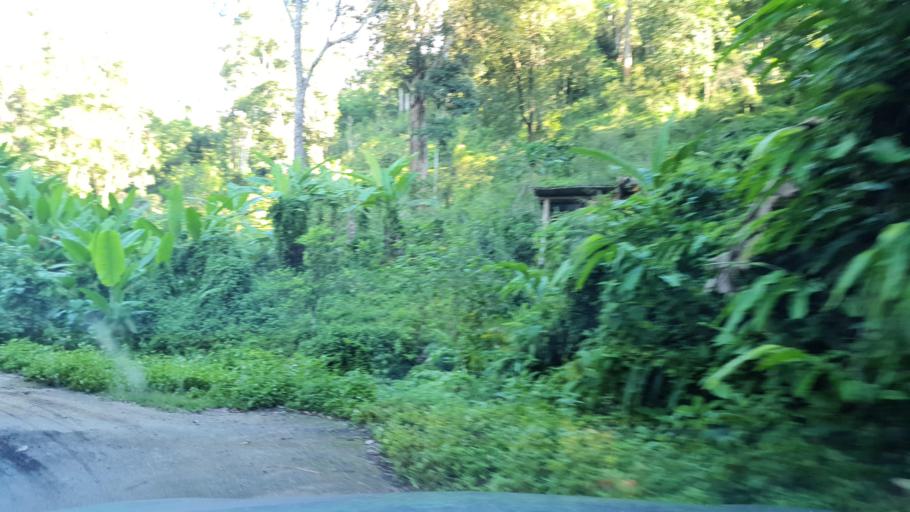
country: TH
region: Chiang Mai
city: Mae On
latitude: 18.8150
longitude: 99.3440
